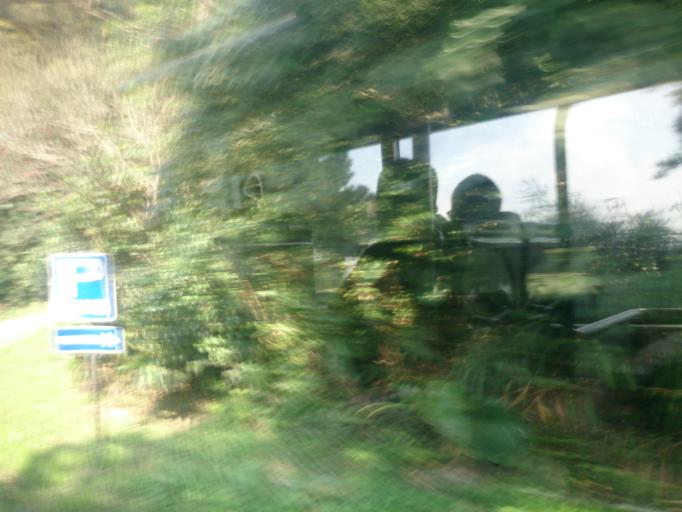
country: TW
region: Taipei
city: Taipei
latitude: 25.1792
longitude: 121.5443
